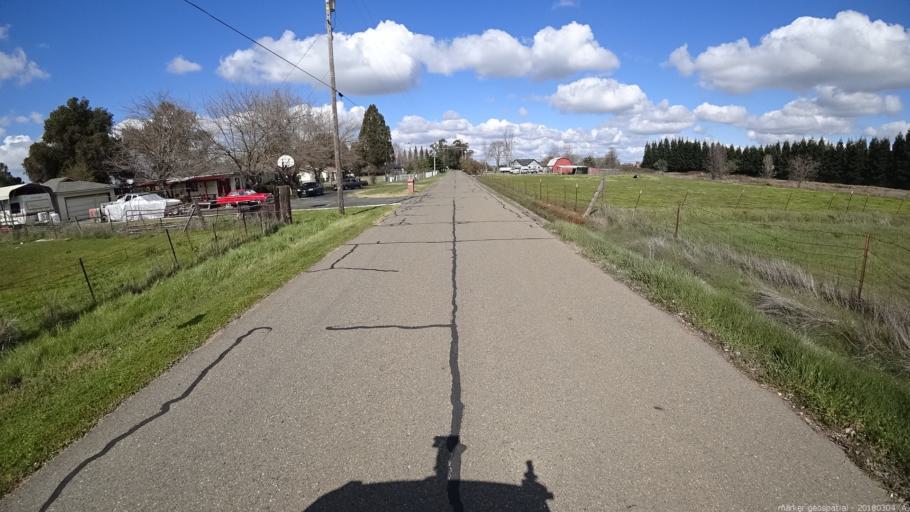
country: US
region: California
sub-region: Sacramento County
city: Vineyard
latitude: 38.4797
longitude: -121.3023
